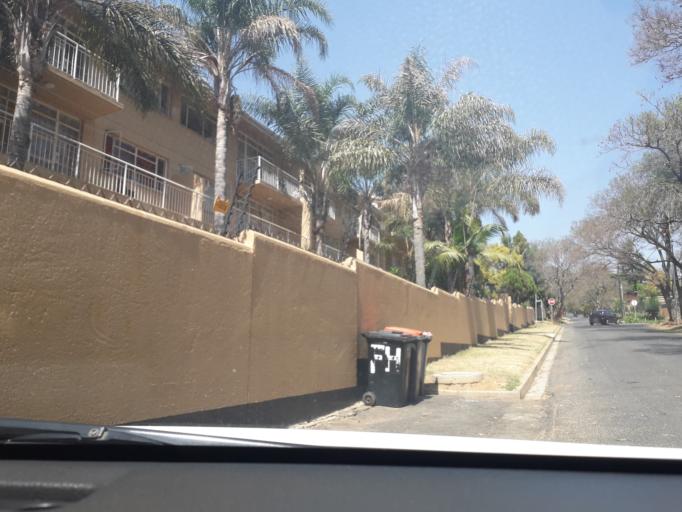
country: ZA
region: Gauteng
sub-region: City of Johannesburg Metropolitan Municipality
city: Roodepoort
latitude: -26.1051
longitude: 27.9731
